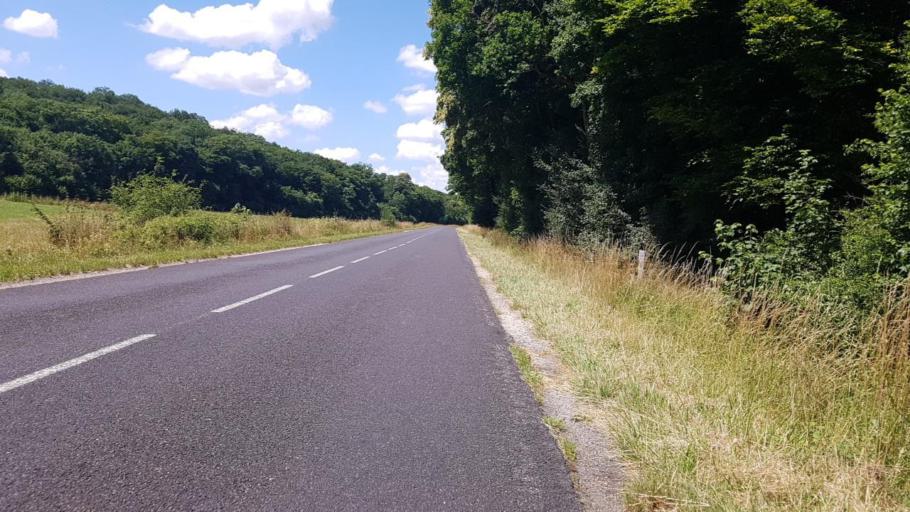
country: FR
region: Lorraine
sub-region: Departement de la Meuse
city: Vacon
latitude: 48.6715
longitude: 5.5696
